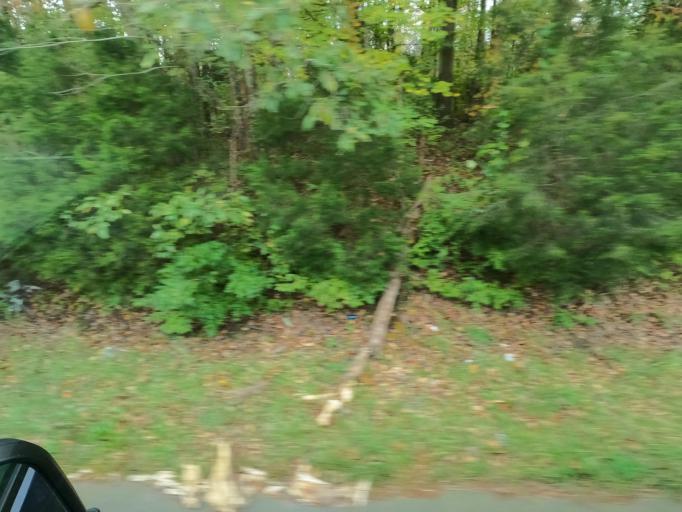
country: US
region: Tennessee
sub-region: Cheatham County
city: Pegram
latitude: 36.0971
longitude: -87.0314
